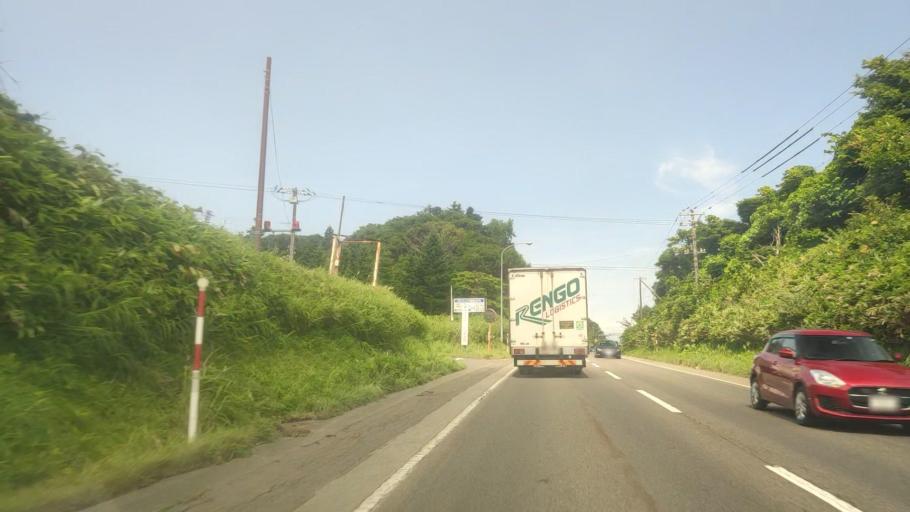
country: JP
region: Hokkaido
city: Nanae
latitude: 42.1677
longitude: 140.4610
